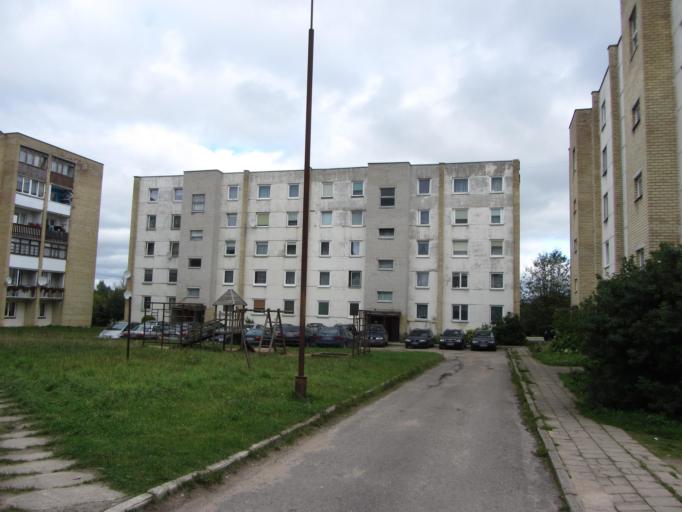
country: LT
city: Salcininkai
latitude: 54.3142
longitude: 25.3820
